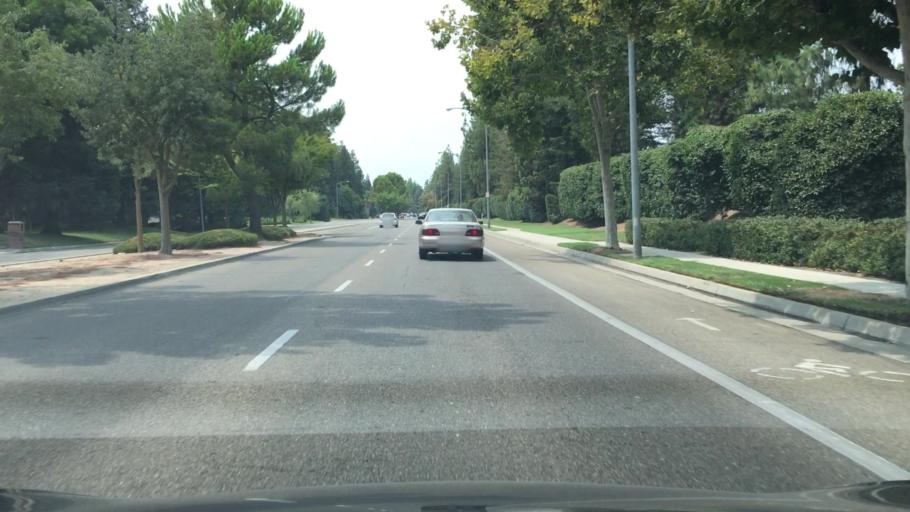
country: US
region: California
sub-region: Fresno County
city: Clovis
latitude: 36.8665
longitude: -119.7733
